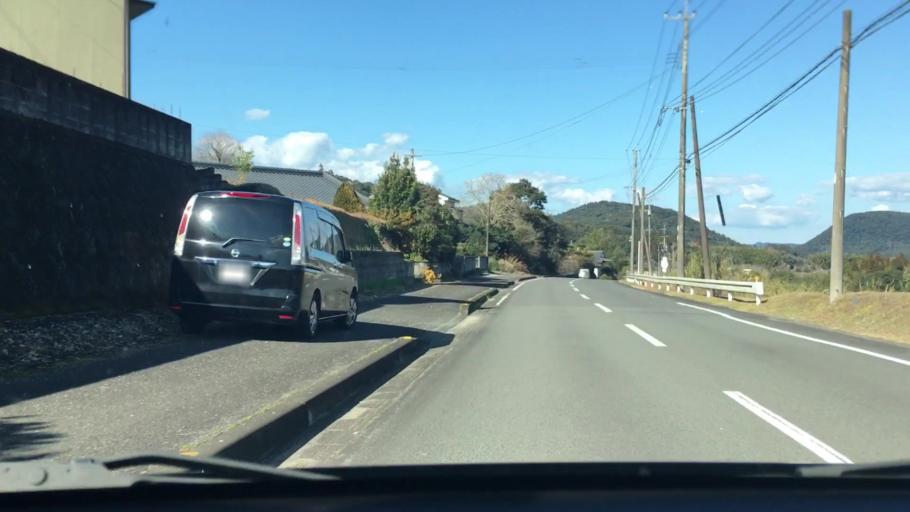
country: JP
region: Kagoshima
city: Satsumasendai
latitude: 31.7717
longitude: 130.4014
